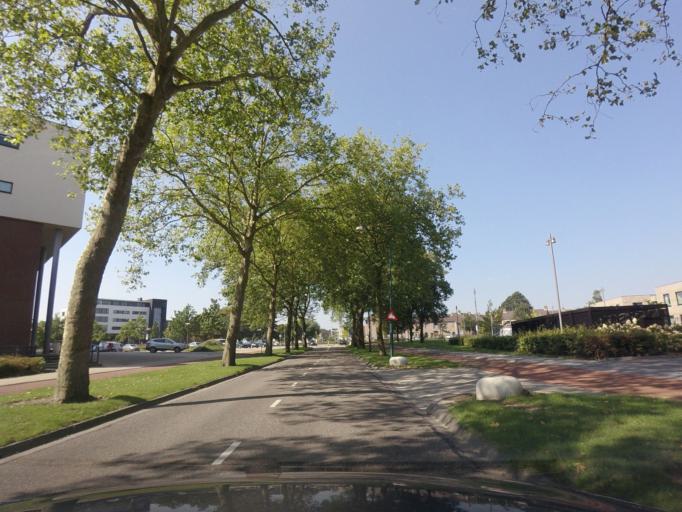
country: NL
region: North Brabant
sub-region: Gemeente Moerdijk
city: Klundert
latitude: 51.6421
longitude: 4.6057
